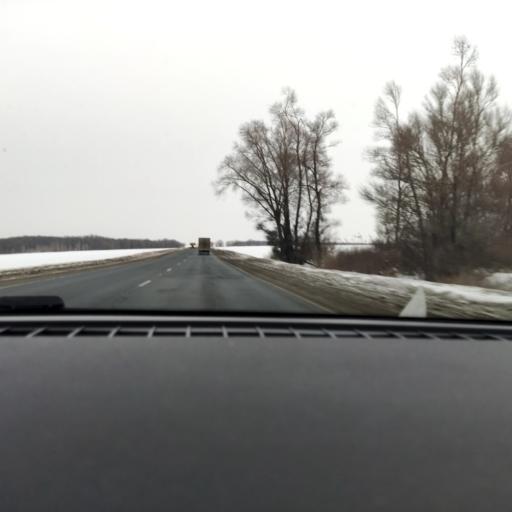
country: RU
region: Samara
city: Petra-Dubrava
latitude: 53.3150
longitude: 50.4564
